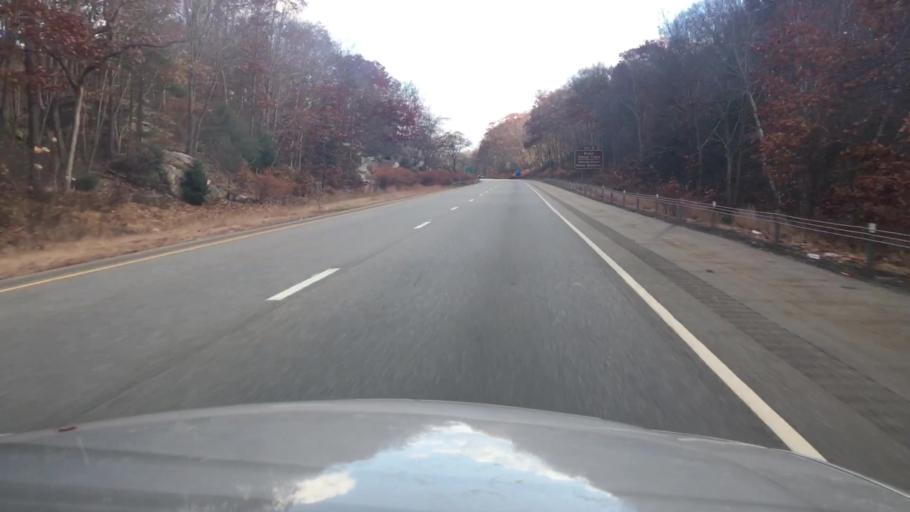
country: US
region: Connecticut
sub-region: Middlesex County
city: Essex Village
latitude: 41.3585
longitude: -72.4194
